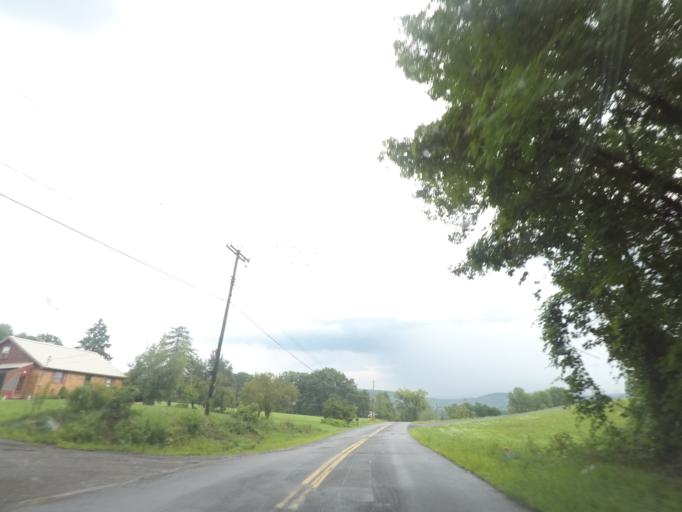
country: US
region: New York
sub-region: Rensselaer County
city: Poestenkill
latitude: 42.7227
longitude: -73.5838
